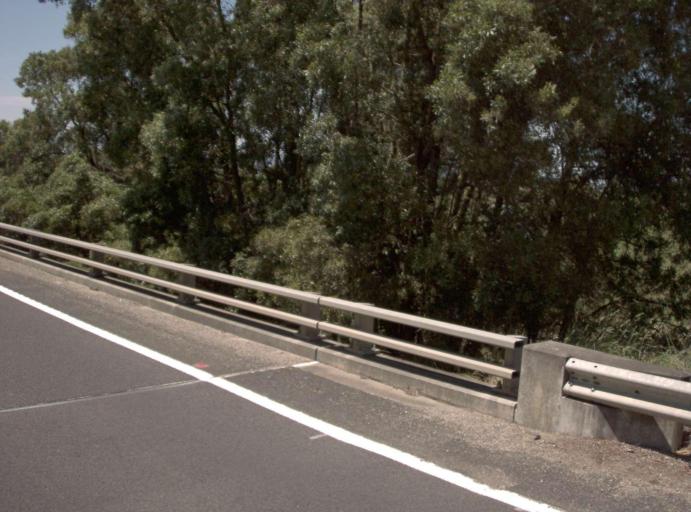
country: AU
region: Victoria
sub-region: East Gippsland
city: Lakes Entrance
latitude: -37.7287
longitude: 148.4439
